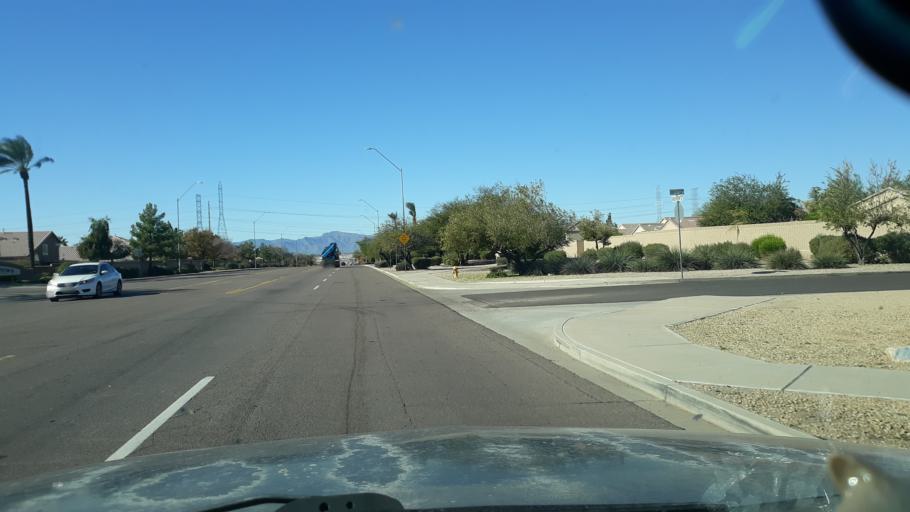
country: US
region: Arizona
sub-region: Maricopa County
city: Youngtown
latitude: 33.5513
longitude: -112.2937
